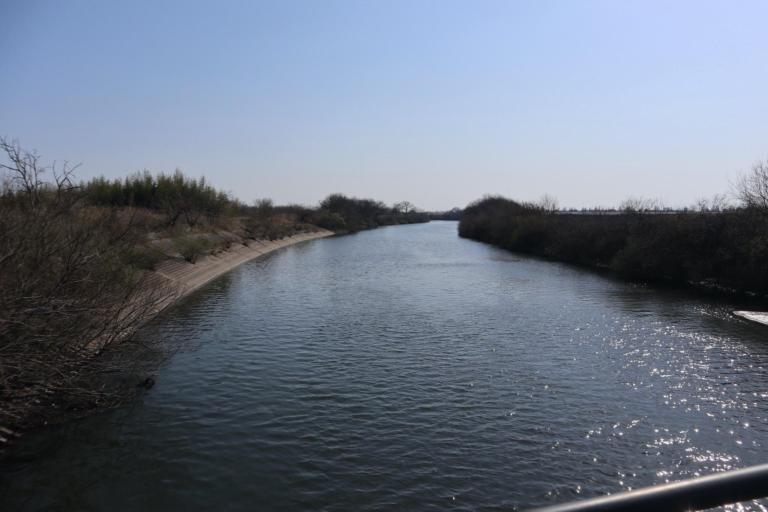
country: JP
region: Tochigi
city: Fujioka
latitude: 36.2568
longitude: 139.6736
